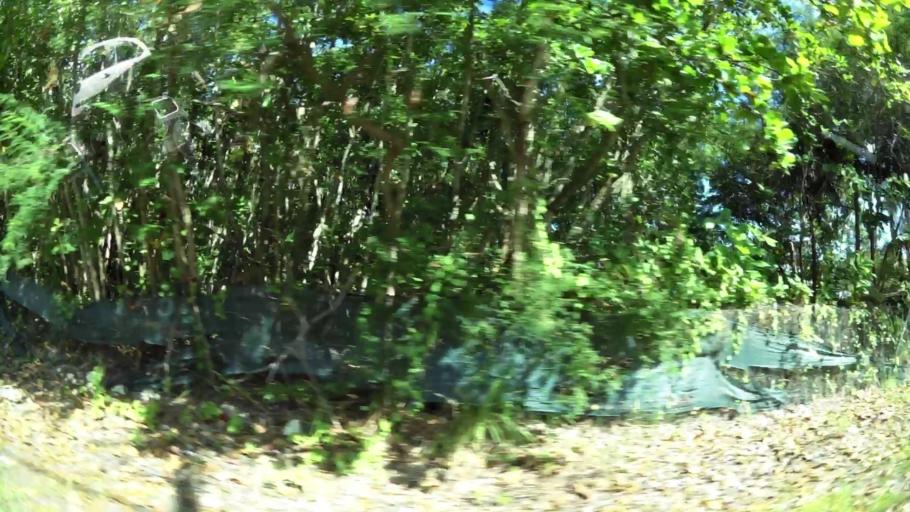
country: GP
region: Guadeloupe
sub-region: Guadeloupe
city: Sainte-Anne
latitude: 16.2277
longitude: -61.3756
